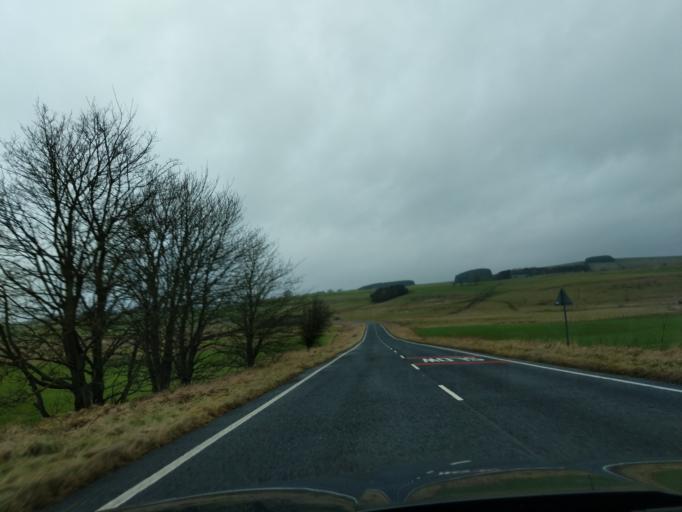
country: GB
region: England
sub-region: Northumberland
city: Otterburn
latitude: 55.2210
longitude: -2.1382
